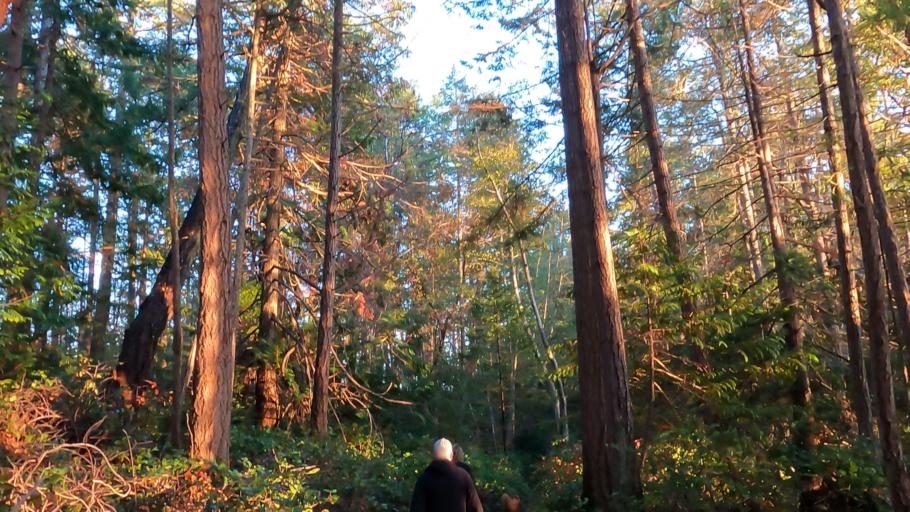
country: CA
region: British Columbia
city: North Cowichan
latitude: 48.9502
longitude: -123.5646
